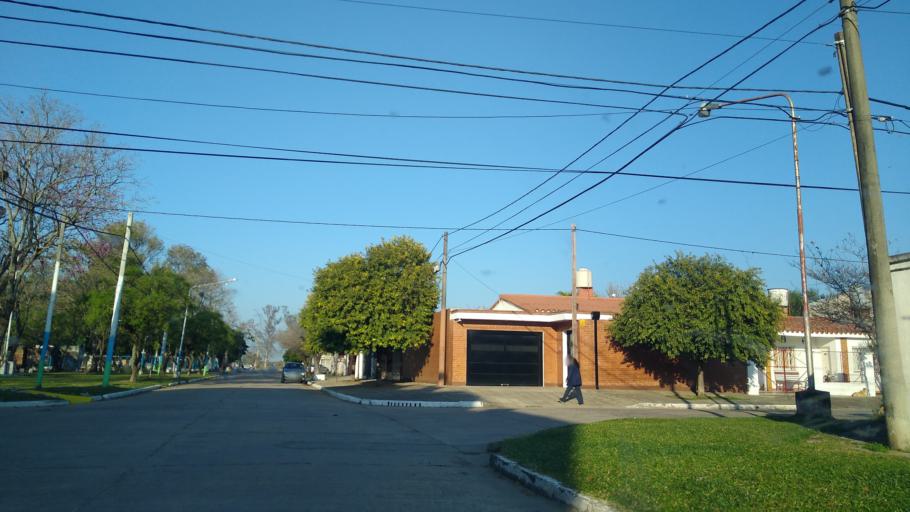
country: AR
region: Chaco
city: Barranqueras
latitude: -27.4809
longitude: -58.9503
